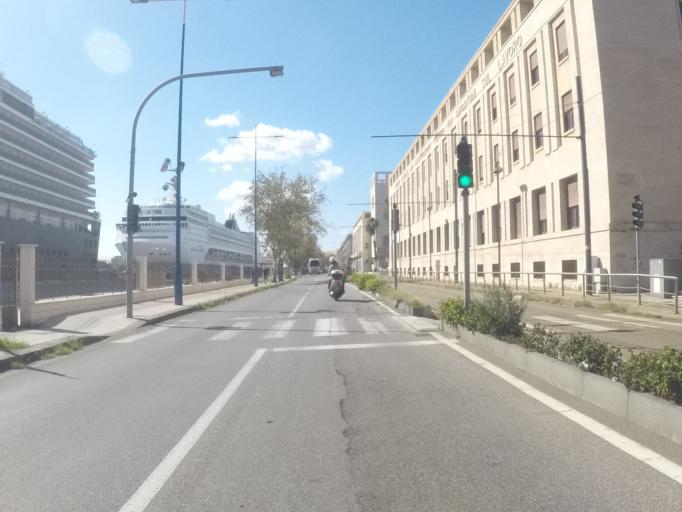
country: IT
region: Sicily
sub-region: Messina
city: Messina
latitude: 38.1950
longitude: 15.5575
